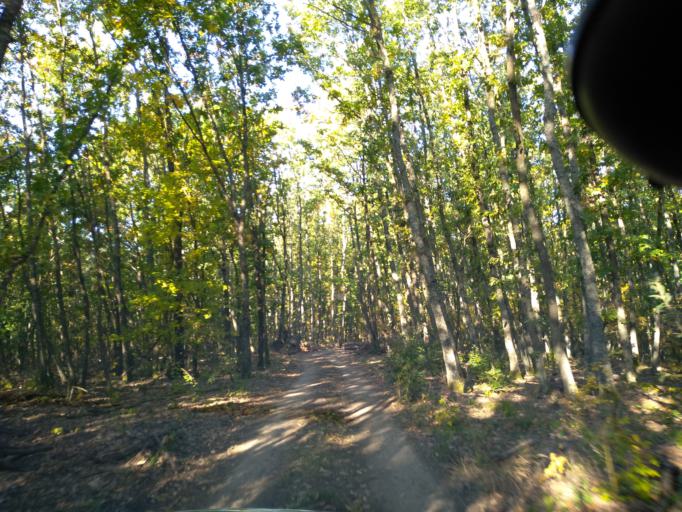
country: RO
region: Timis
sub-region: Comuna Bogda
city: Bogda
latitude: 45.9229
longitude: 21.6172
